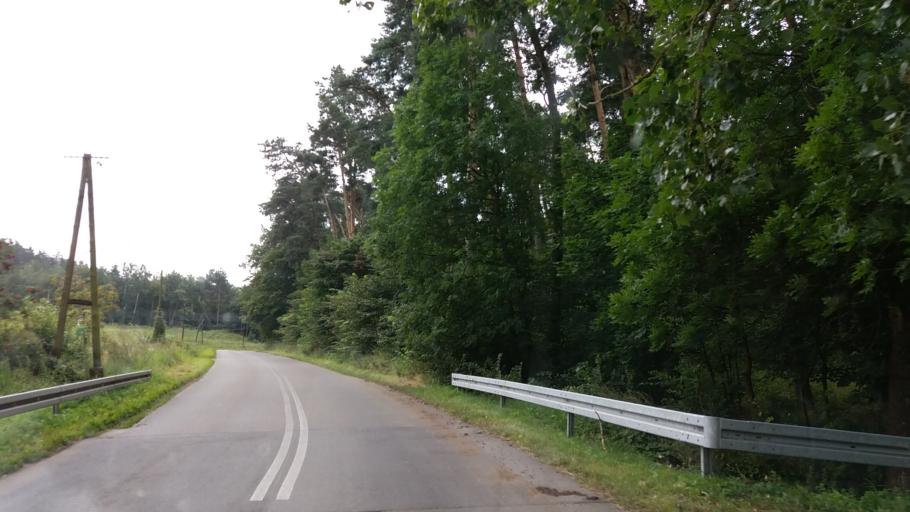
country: PL
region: West Pomeranian Voivodeship
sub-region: Powiat choszczenski
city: Krzecin
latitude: 53.0901
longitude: 15.4740
